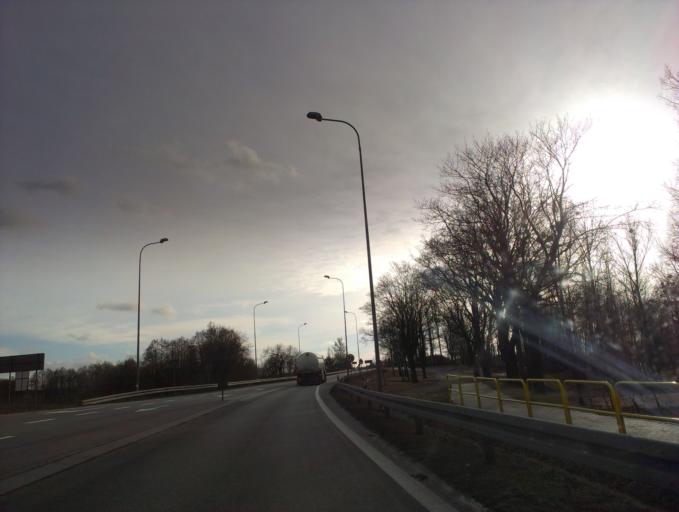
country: PL
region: Kujawsko-Pomorskie
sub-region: Powiat lipnowski
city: Kikol
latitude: 52.9088
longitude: 19.1200
